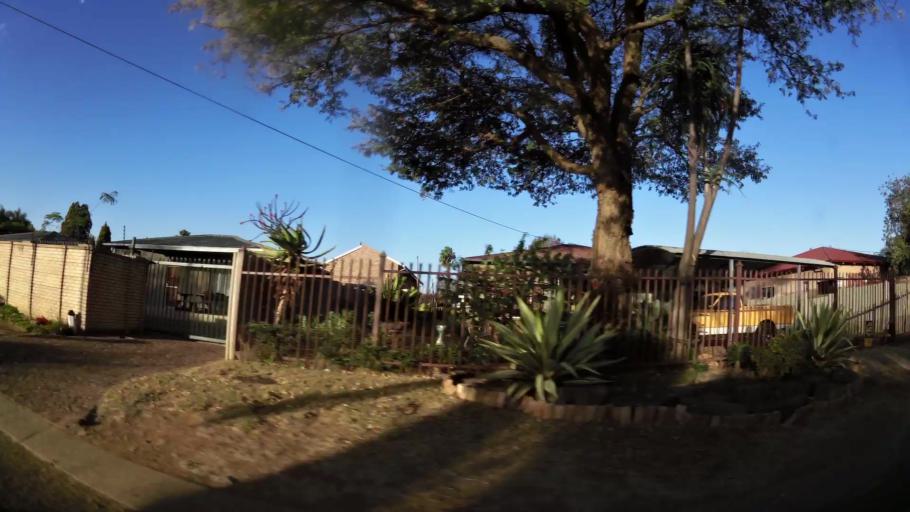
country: ZA
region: Gauteng
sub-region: City of Tshwane Metropolitan Municipality
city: Pretoria
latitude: -25.7070
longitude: 28.2362
